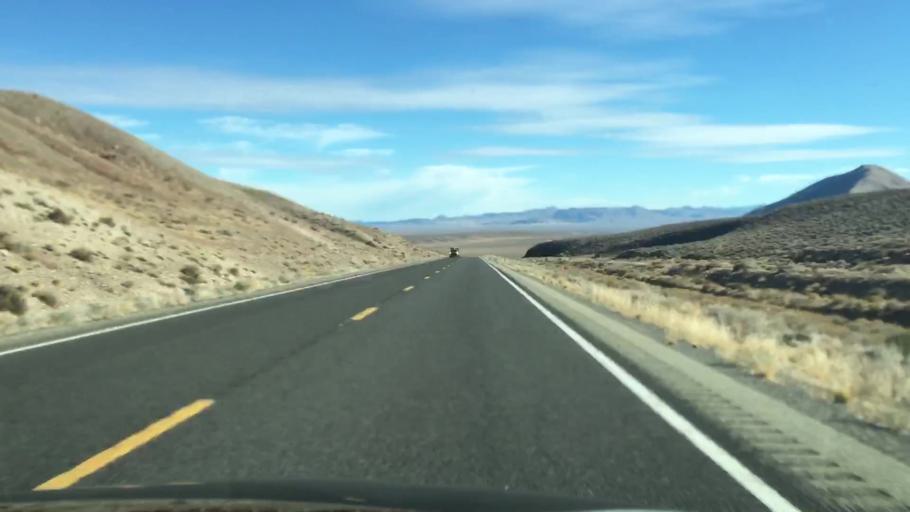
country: US
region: Nevada
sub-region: Lyon County
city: Yerington
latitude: 39.0379
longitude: -118.9326
